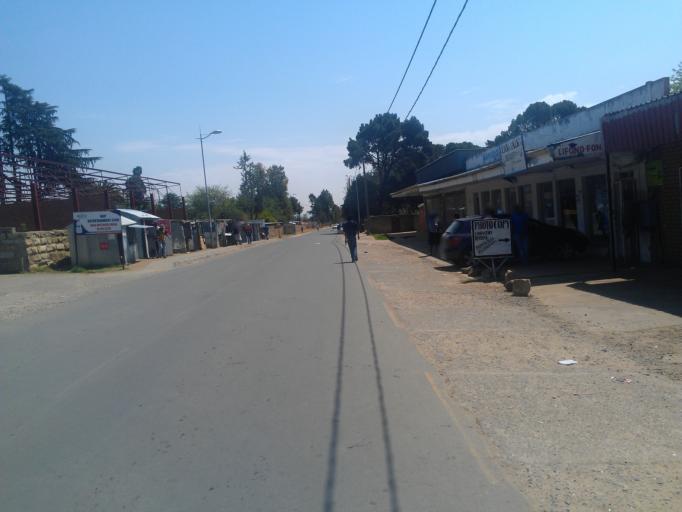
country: LS
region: Berea
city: Teyateyaneng
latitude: -29.1497
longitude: 27.7418
